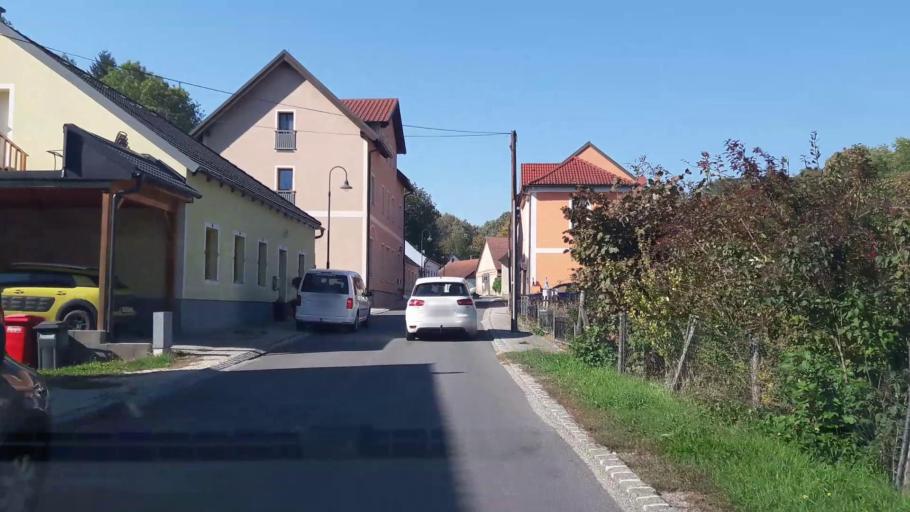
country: AT
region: Lower Austria
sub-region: Politischer Bezirk Korneuburg
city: Ernstbrunn
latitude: 48.5415
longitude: 16.3527
